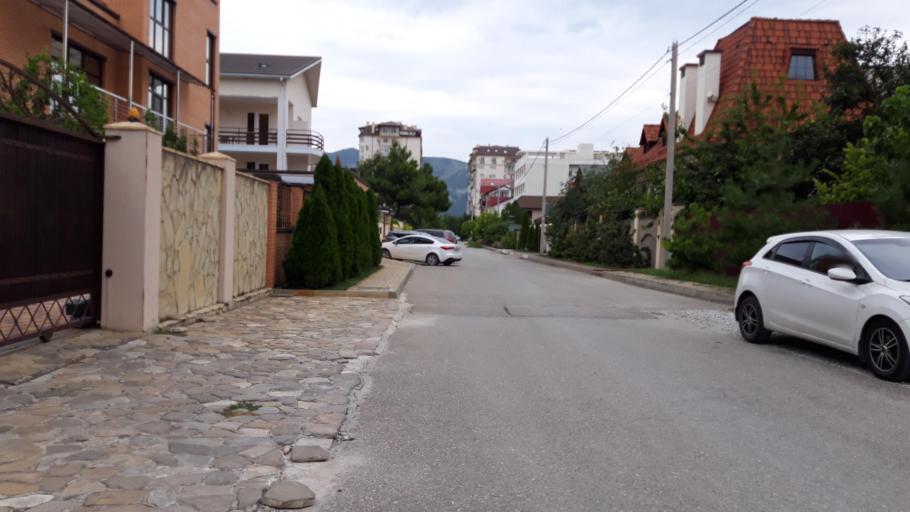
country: RU
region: Krasnodarskiy
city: Gelendzhik
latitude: 44.5503
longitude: 38.0556
